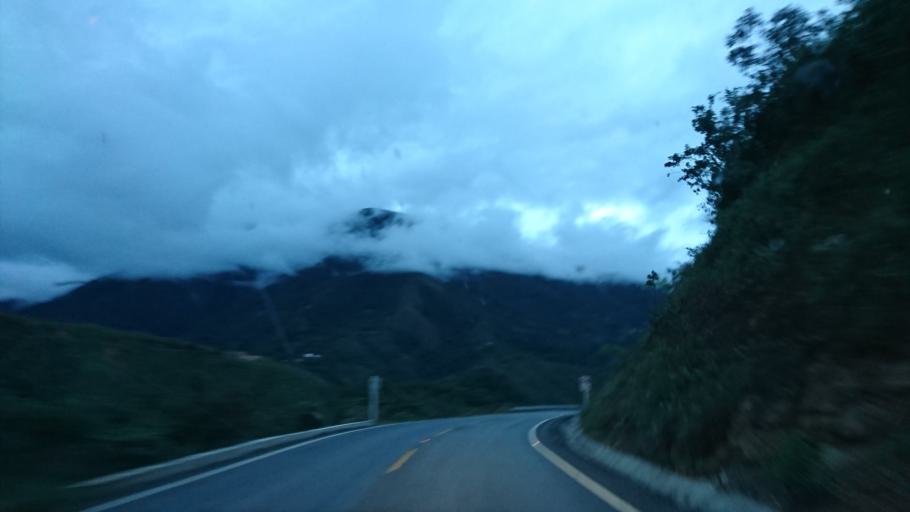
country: BO
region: La Paz
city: Coroico
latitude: -16.2023
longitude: -67.7414
